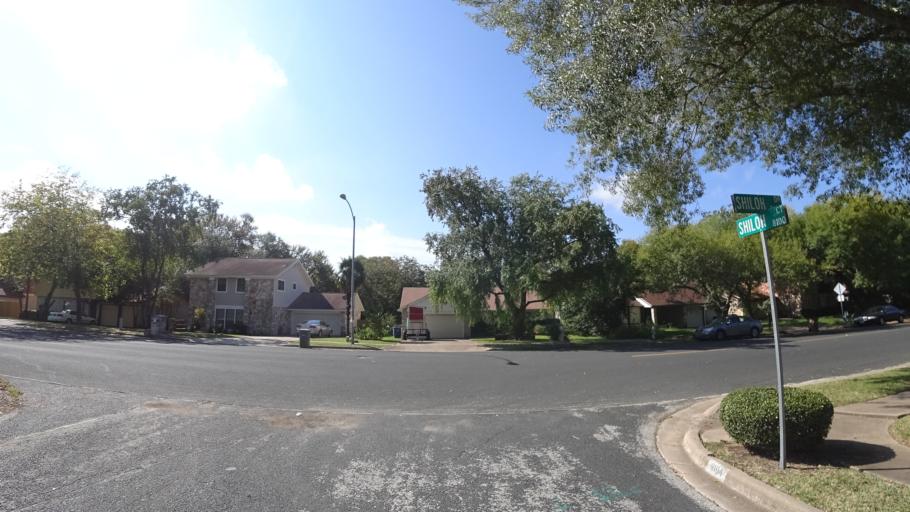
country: US
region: Texas
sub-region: Travis County
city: Shady Hollow
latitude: 30.1957
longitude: -97.8205
